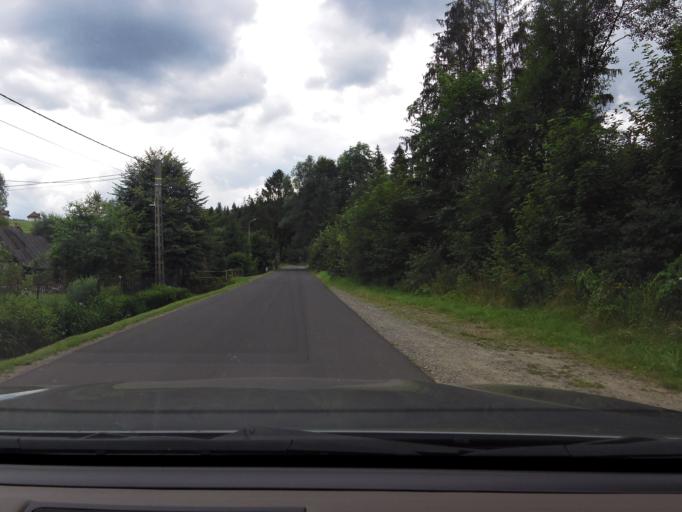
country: PL
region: Silesian Voivodeship
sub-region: Powiat zywiecki
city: Ujsoly
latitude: 49.4671
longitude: 19.1514
